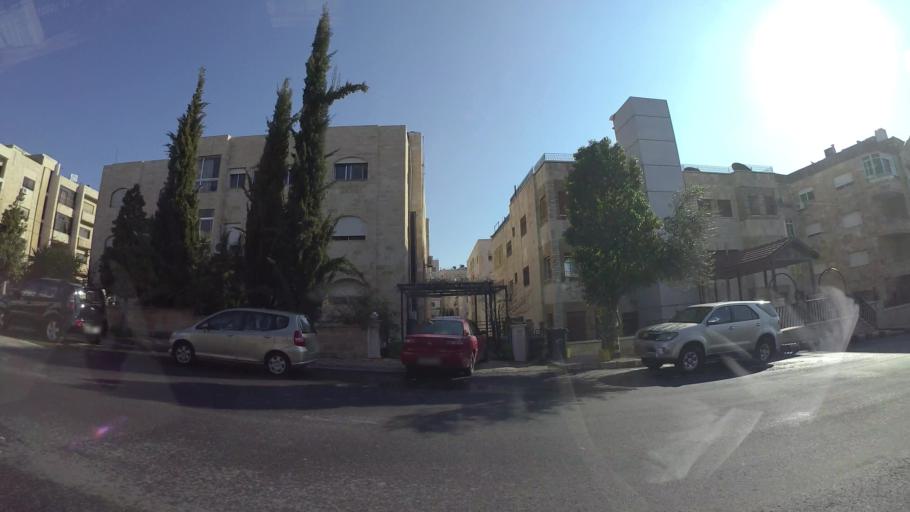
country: JO
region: Amman
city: Al Jubayhah
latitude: 31.9997
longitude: 35.8863
